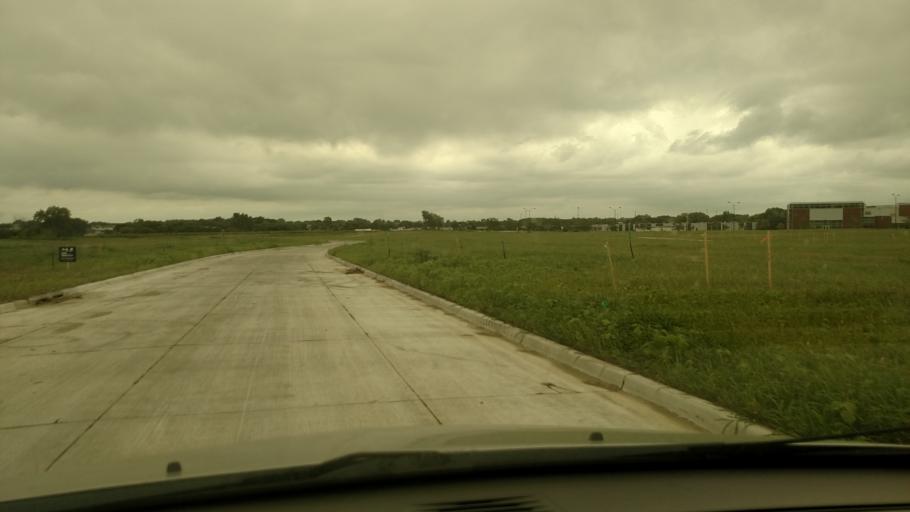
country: US
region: Iowa
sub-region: Polk County
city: Ankeny
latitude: 41.7144
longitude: -93.6123
